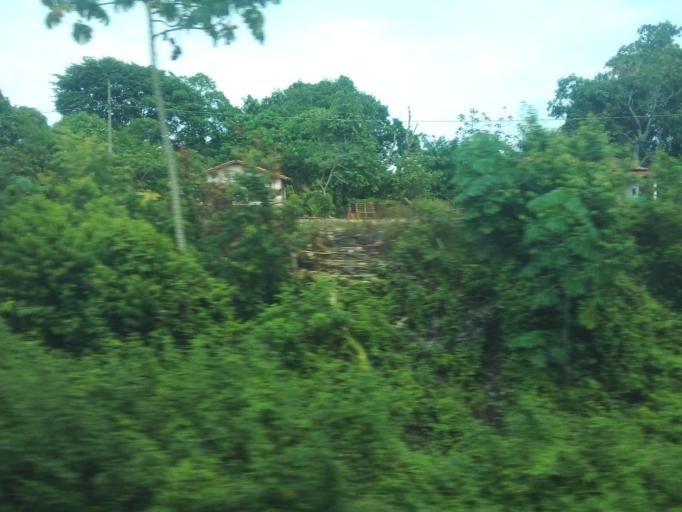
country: BR
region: Maranhao
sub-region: Anajatuba
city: Anajatuba
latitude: -3.3486
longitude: -44.5034
